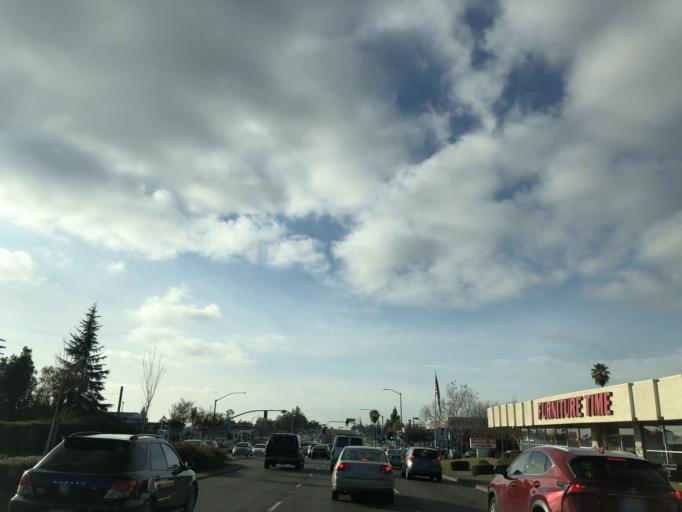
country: US
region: California
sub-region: Sacramento County
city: Foothill Farms
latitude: 38.6610
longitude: -121.3538
